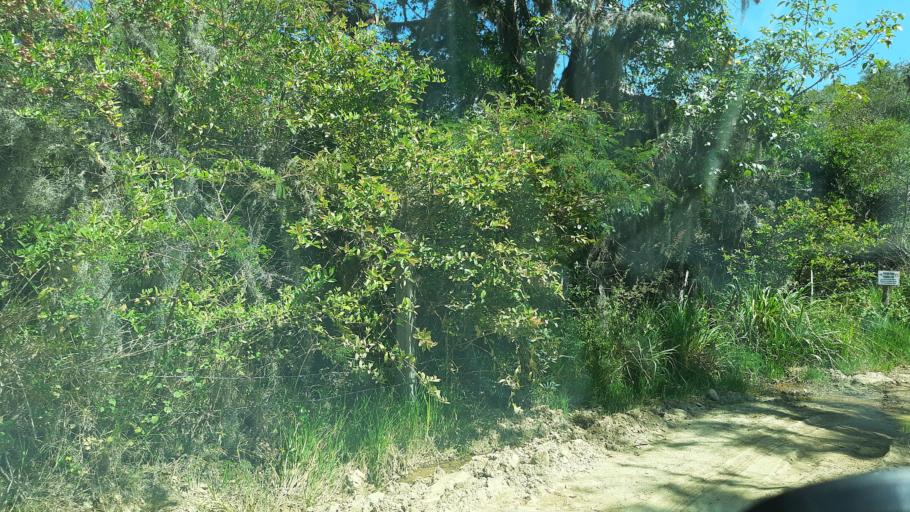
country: CO
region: Boyaca
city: Santa Sofia
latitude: 5.6965
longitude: -73.5770
